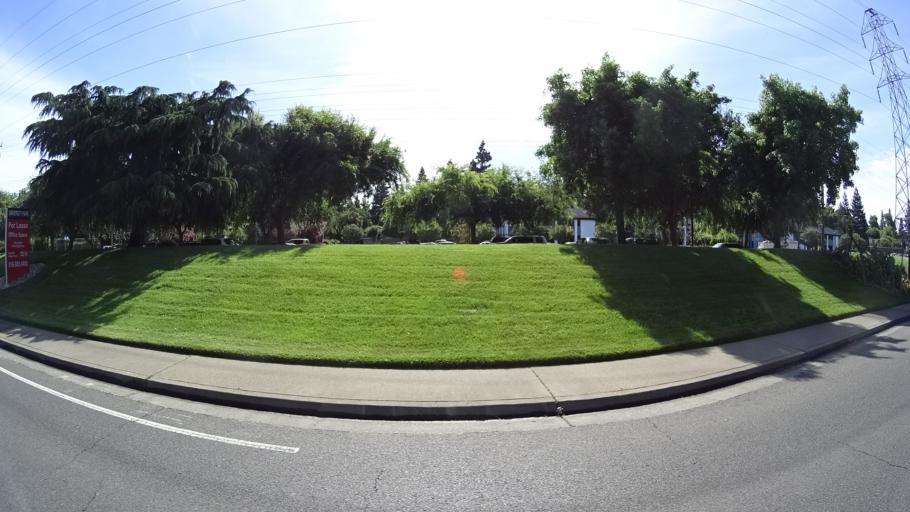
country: US
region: California
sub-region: Sacramento County
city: Rosemont
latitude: 38.5659
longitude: -121.4090
